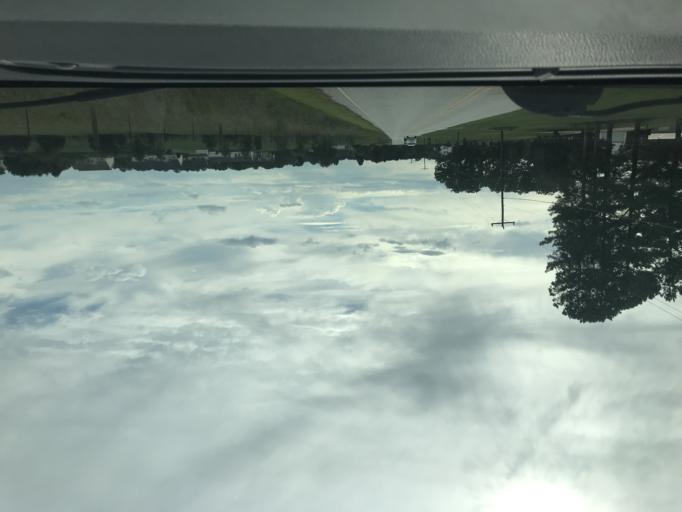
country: US
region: South Carolina
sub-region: Cherokee County
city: Gaffney
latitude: 35.1369
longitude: -81.6815
